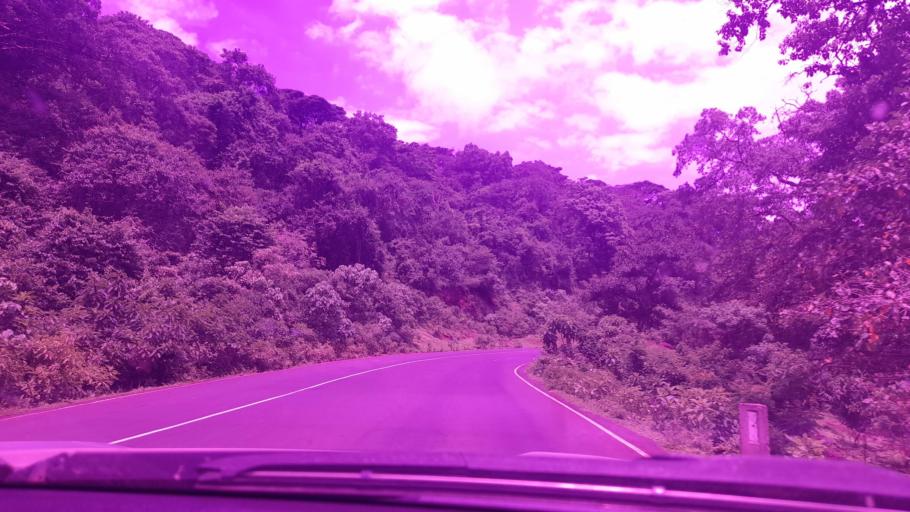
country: ET
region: Oromiya
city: Metu
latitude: 8.3384
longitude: 35.7445
